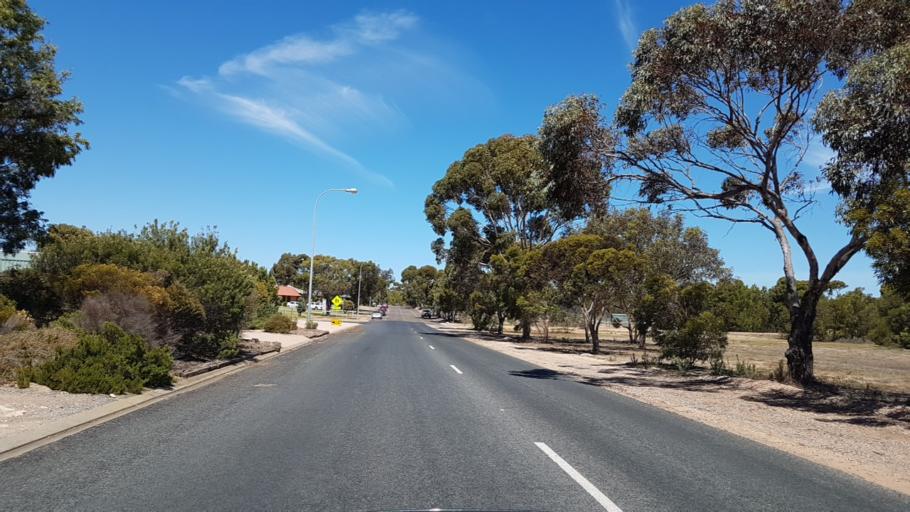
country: AU
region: South Australia
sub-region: Copper Coast
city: Wallaroo
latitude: -34.0603
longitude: 137.5879
